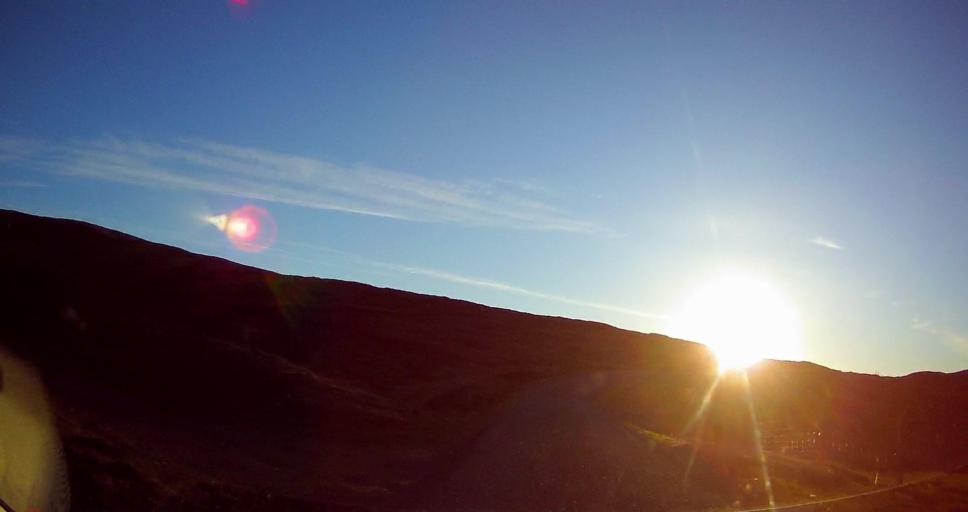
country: GB
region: Scotland
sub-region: Shetland Islands
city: Lerwick
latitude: 60.4404
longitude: -1.3996
